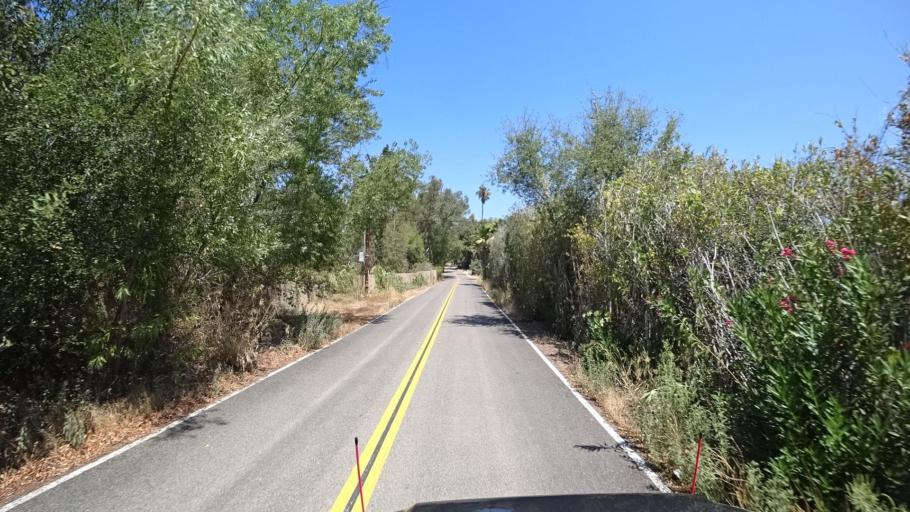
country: US
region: California
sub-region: San Diego County
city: Fallbrook
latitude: 33.4541
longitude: -117.2699
